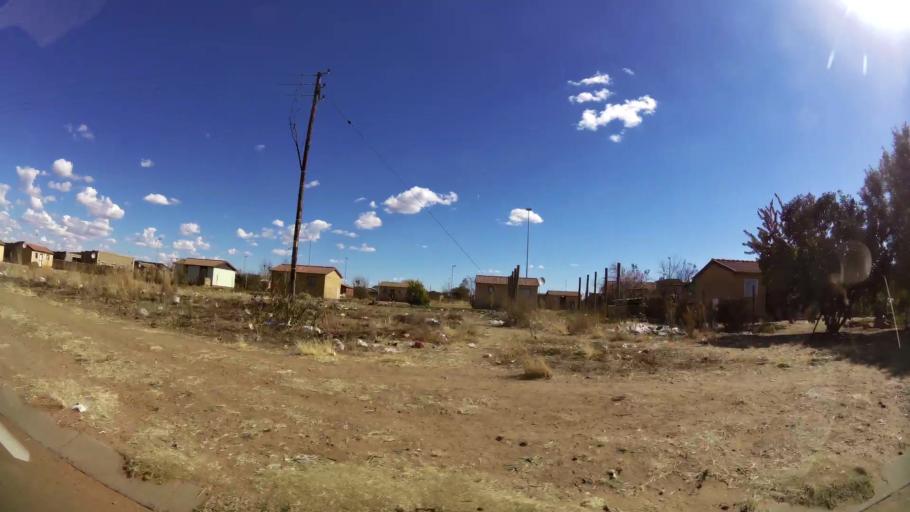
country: ZA
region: North-West
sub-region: Dr Kenneth Kaunda District Municipality
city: Klerksdorp
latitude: -26.8731
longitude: 26.5746
